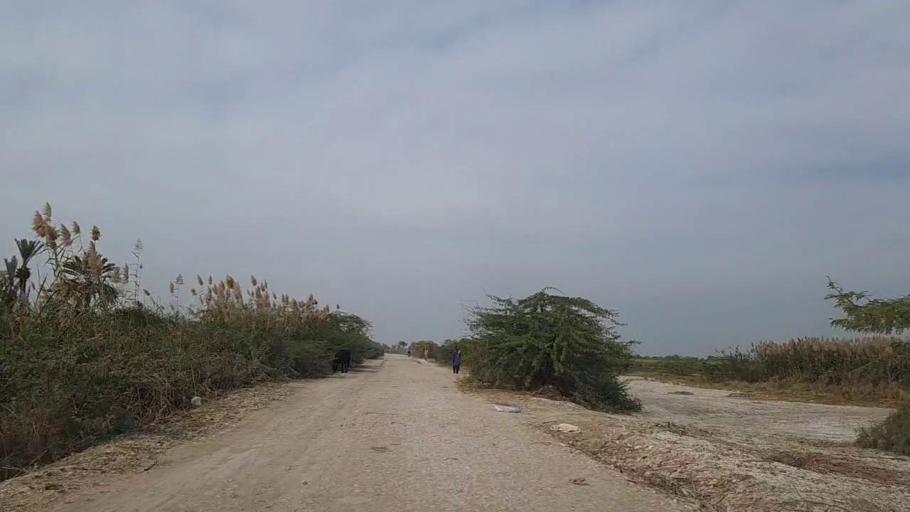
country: PK
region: Sindh
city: Daur
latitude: 26.4038
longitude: 68.4384
